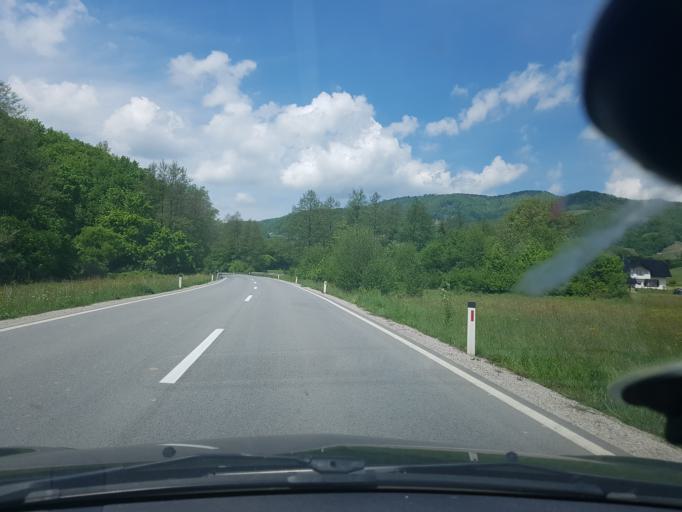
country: SI
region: Rogaska Slatina
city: Rogaska Slatina
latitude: 46.2453
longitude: 15.6526
